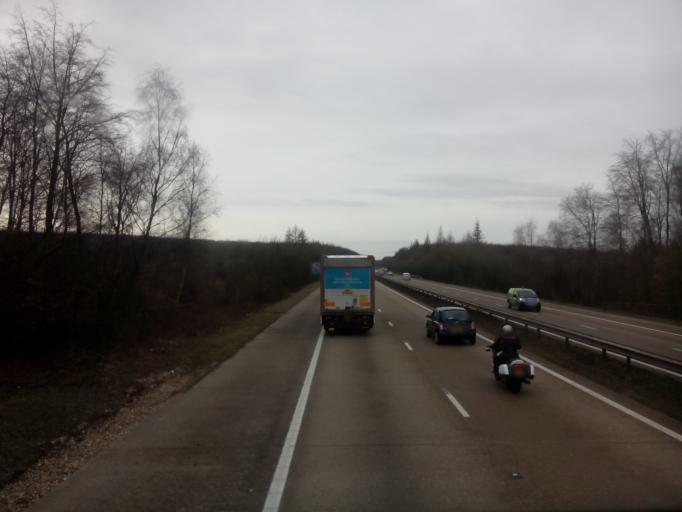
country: GB
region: England
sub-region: Hampshire
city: Kings Worthy
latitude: 51.1265
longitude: -1.2496
